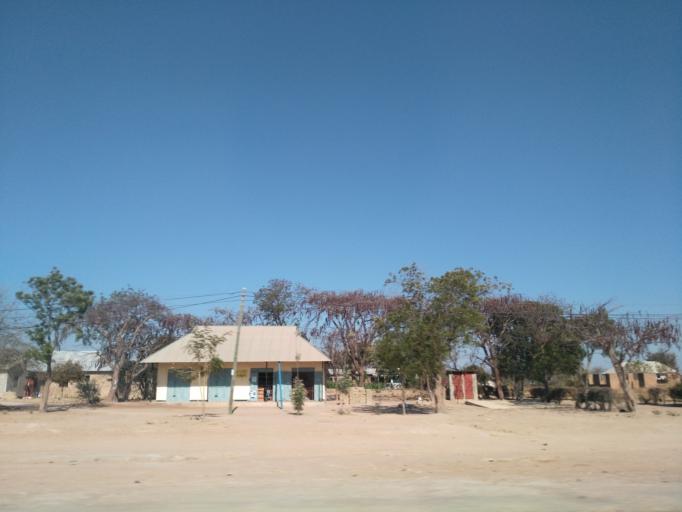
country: TZ
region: Dodoma
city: Dodoma
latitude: -6.1137
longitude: 35.7477
